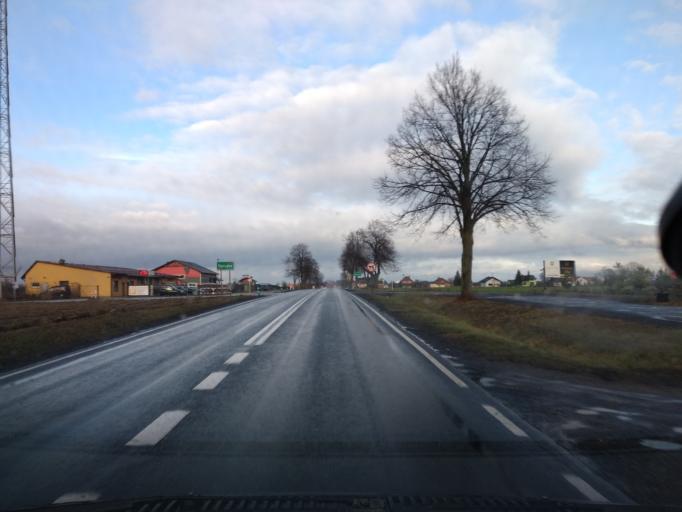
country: PL
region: Greater Poland Voivodeship
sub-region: Powiat koninski
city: Rychwal
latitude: 52.0538
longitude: 18.1631
